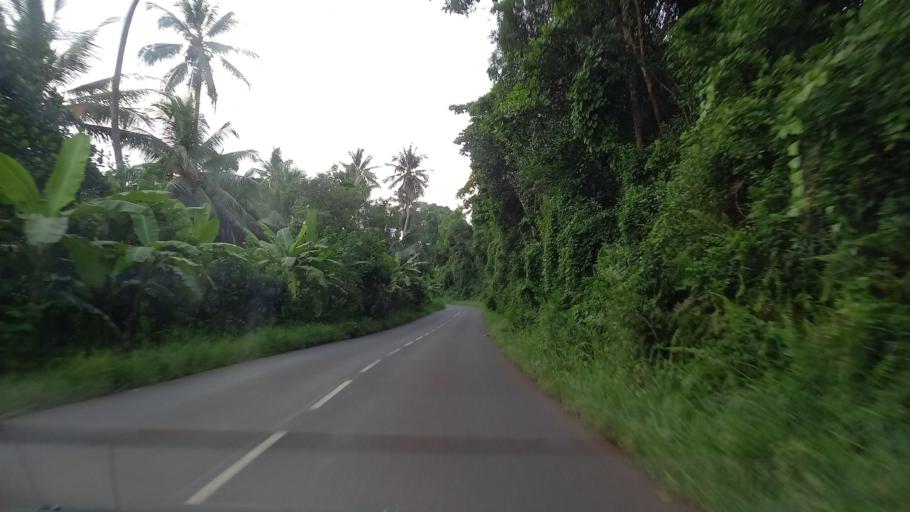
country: YT
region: M'Tsangamouji
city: M'Tsangamouji
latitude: -12.7615
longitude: 45.1023
